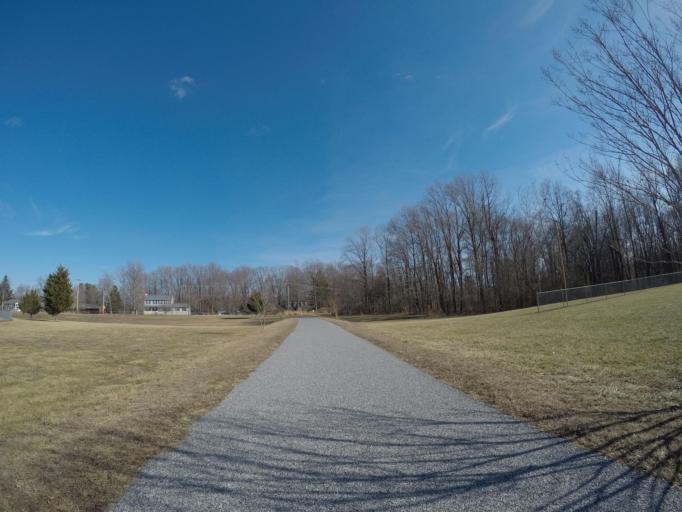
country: US
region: Maryland
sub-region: Charles County
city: Bennsville
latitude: 38.5983
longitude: -77.0179
